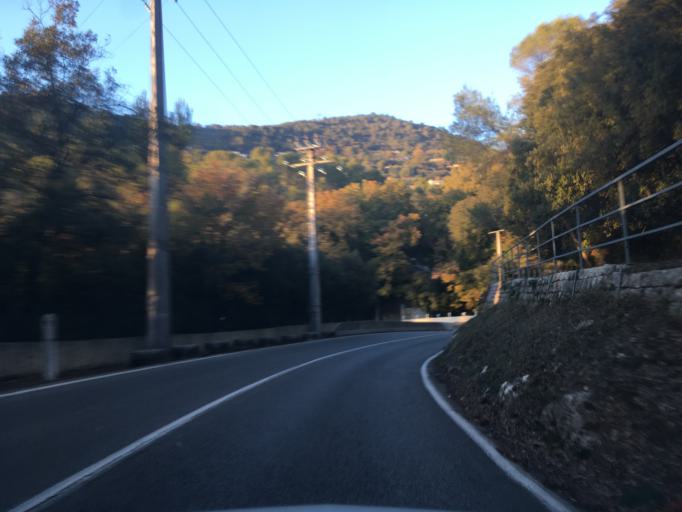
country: FR
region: Provence-Alpes-Cote d'Azur
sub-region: Departement des Alpes-Maritimes
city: Le Tignet
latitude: 43.6321
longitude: 6.8418
